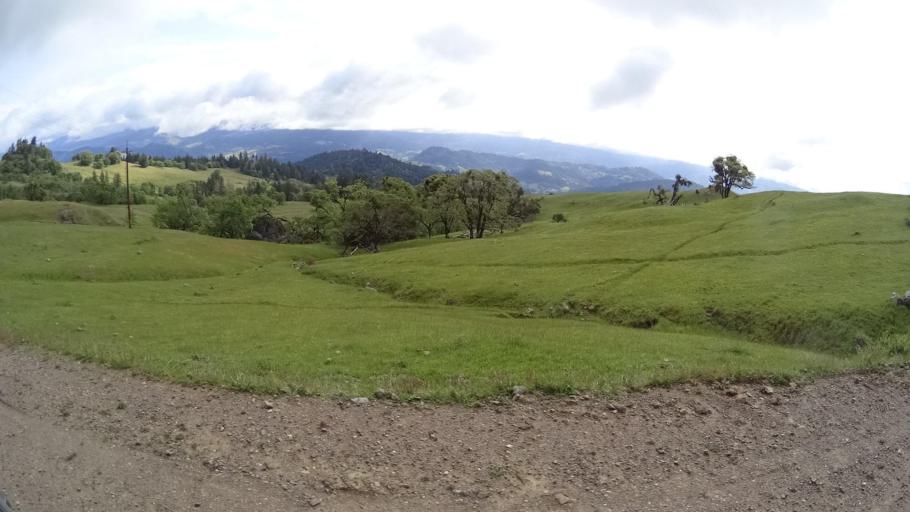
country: US
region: California
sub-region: Humboldt County
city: Redway
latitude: 40.2023
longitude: -123.6941
